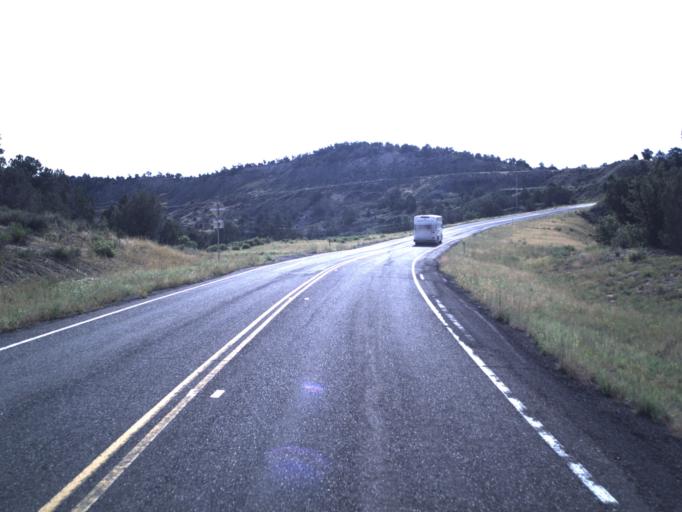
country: US
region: Utah
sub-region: Washington County
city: Hildale
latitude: 37.2629
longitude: -112.7760
